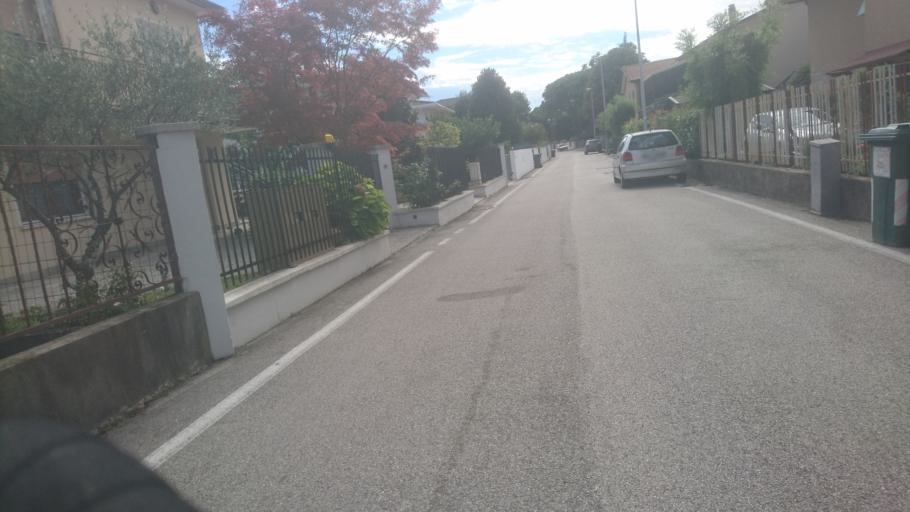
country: IT
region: Veneto
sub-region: Provincia di Venezia
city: Mira Taglio
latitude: 45.4317
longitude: 12.1207
